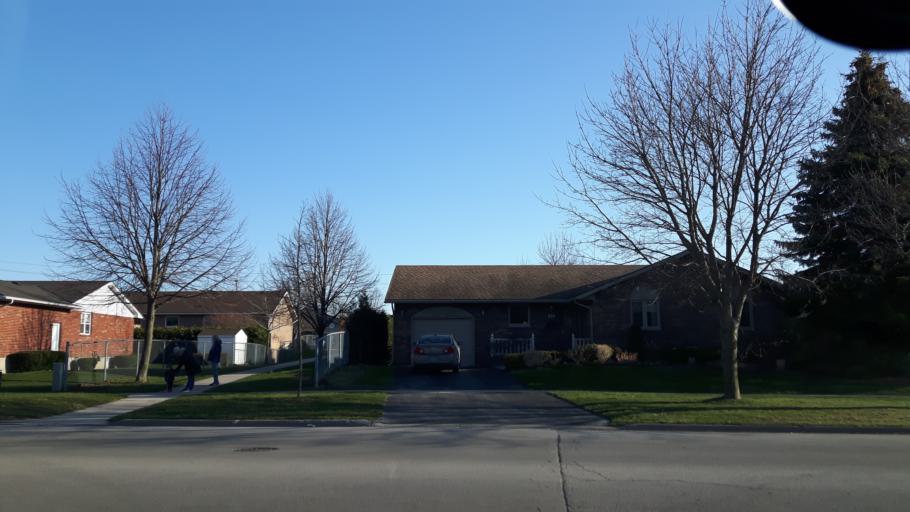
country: CA
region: Ontario
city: Goderich
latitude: 43.7301
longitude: -81.7142
